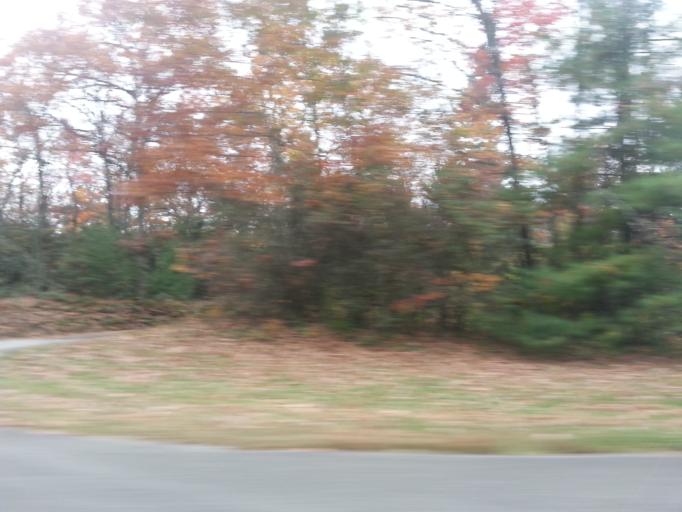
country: US
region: North Carolina
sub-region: Ashe County
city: West Jefferson
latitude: 36.2837
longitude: -81.3881
